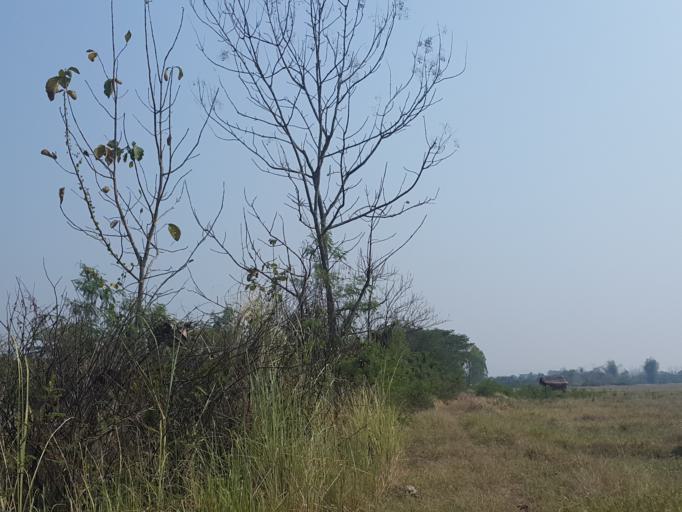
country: TH
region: Chiang Mai
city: San Kamphaeng
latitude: 18.7844
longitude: 99.1344
